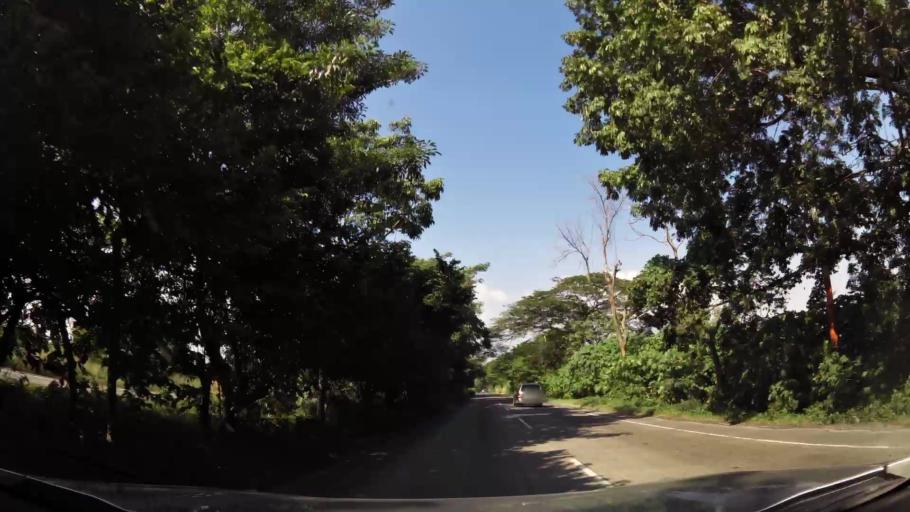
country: GT
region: Escuintla
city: Puerto San Jose
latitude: 13.9809
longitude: -90.7884
